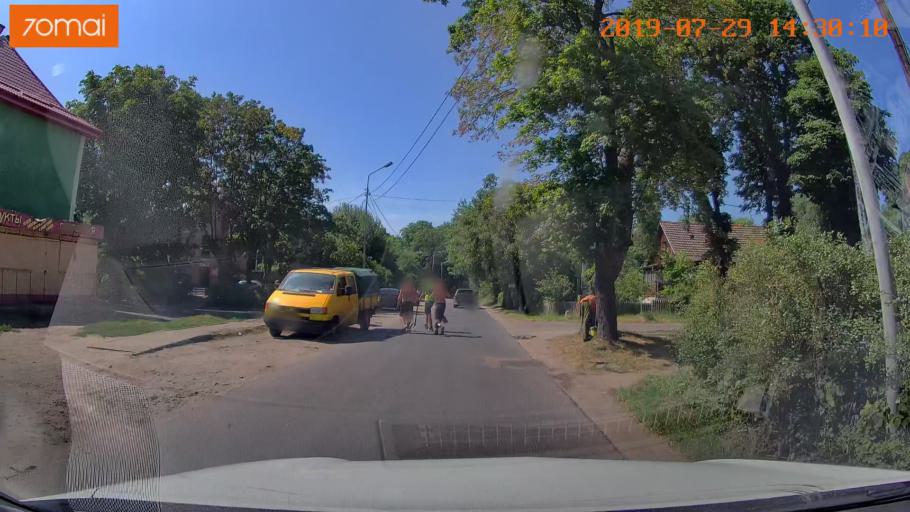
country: RU
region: Kaliningrad
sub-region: Gorod Kaliningrad
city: Baltiysk
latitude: 54.6458
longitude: 19.8893
